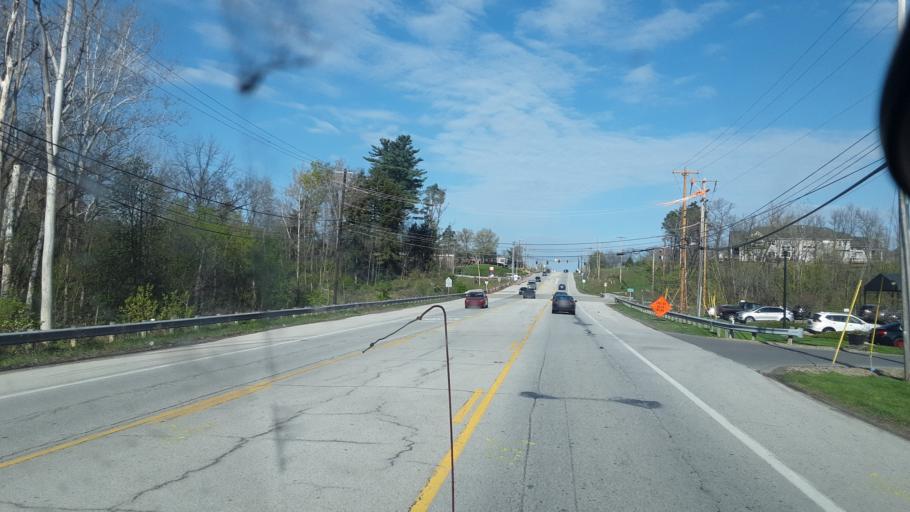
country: US
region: Ohio
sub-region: Medina County
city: Medina
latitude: 41.1369
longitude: -81.8206
